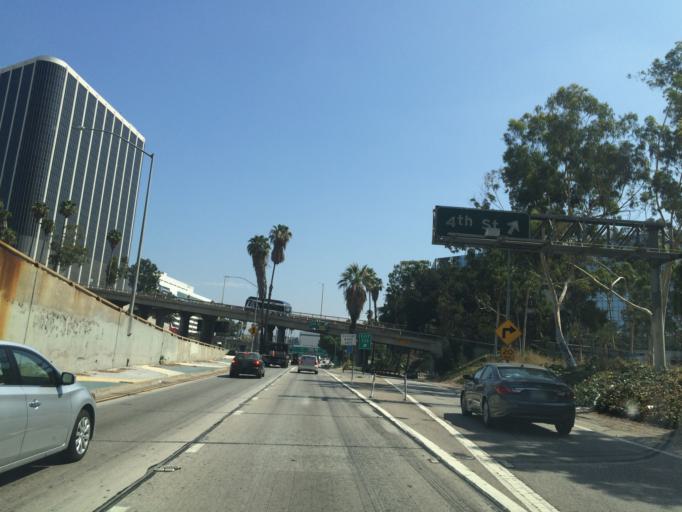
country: US
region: California
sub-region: Los Angeles County
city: Los Angeles
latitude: 34.0536
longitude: -118.2577
